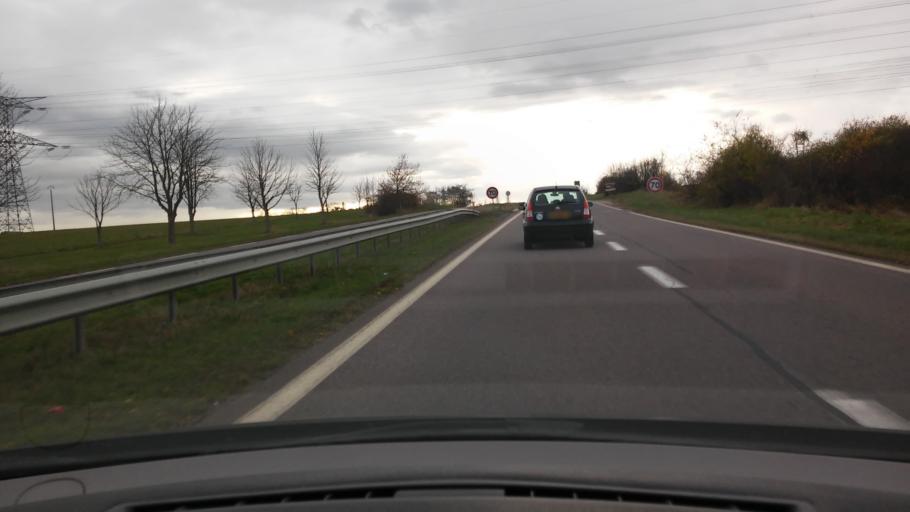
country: FR
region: Lorraine
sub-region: Departement de la Moselle
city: Argancy
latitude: 49.2016
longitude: 6.2088
